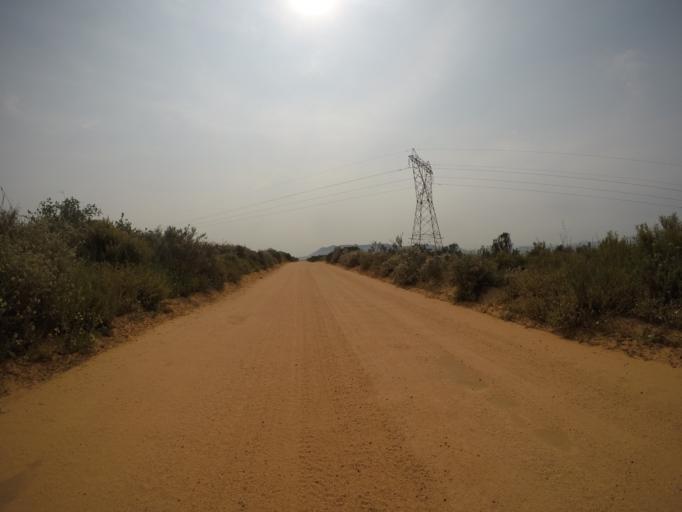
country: ZA
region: Western Cape
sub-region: West Coast District Municipality
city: Malmesbury
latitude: -33.4541
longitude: 18.7427
